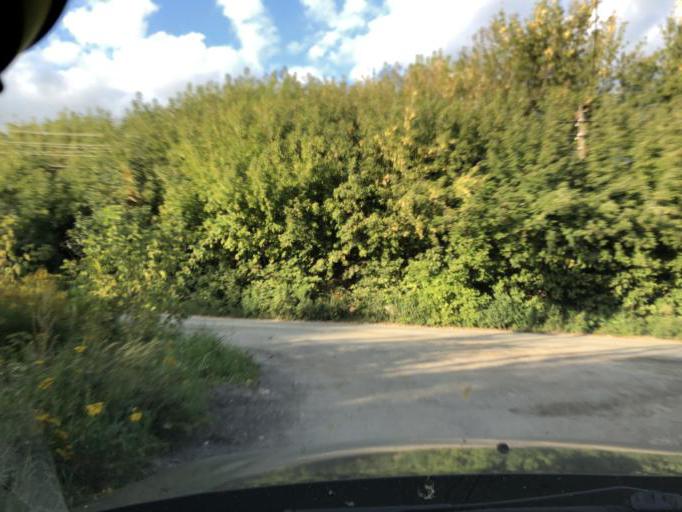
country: RU
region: Tula
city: Kosaya Gora
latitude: 54.1835
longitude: 37.5420
